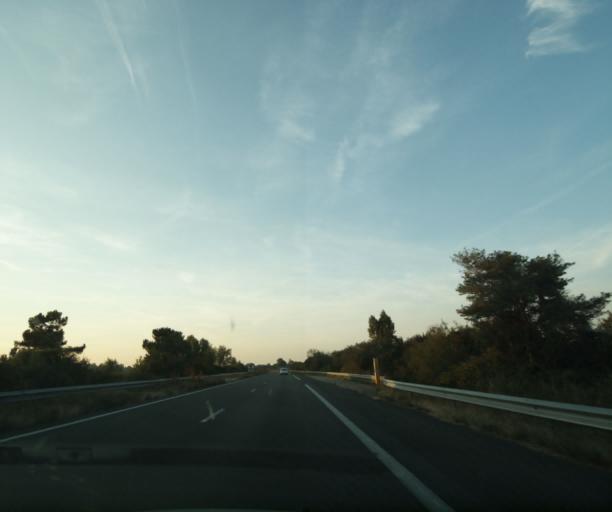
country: FR
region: Aquitaine
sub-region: Departement du Lot-et-Garonne
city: Damazan
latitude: 44.3290
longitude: 0.2577
